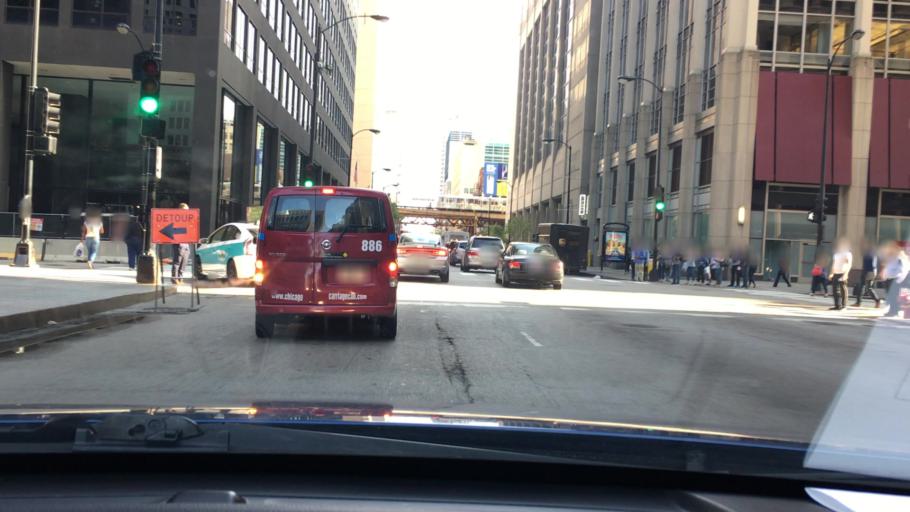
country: US
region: Illinois
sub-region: Cook County
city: Chicago
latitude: 41.8785
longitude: -87.6308
